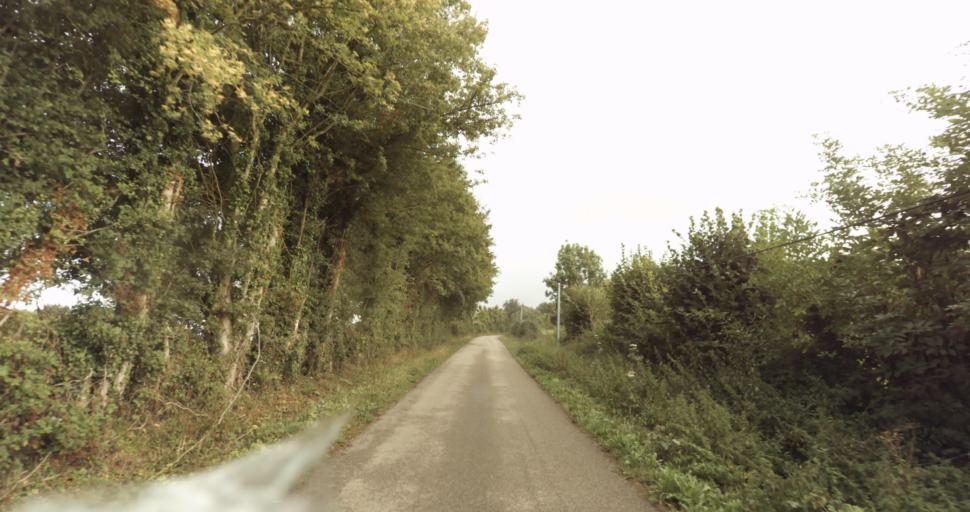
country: FR
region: Lower Normandy
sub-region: Departement de l'Orne
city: Gace
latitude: 48.8709
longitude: 0.2823
